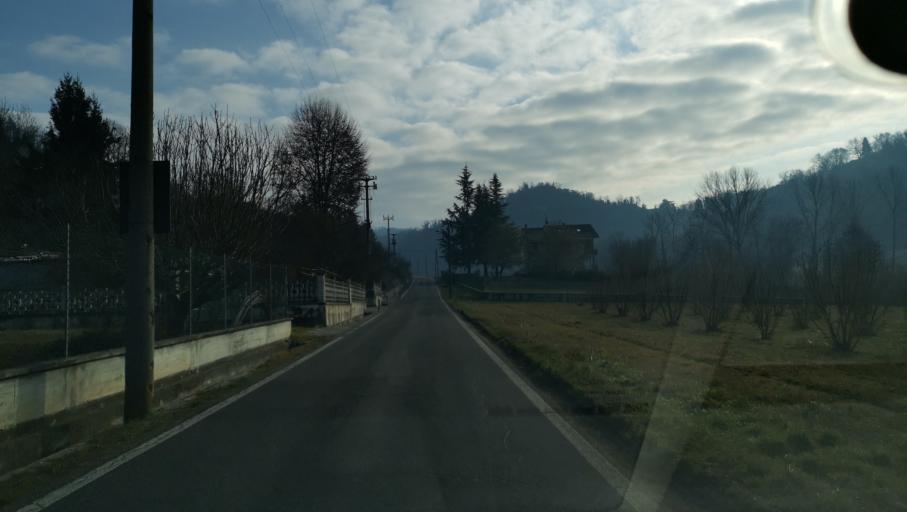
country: IT
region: Piedmont
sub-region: Provincia di Torino
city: San Raffaele Cimena
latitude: 45.1361
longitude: 7.8454
